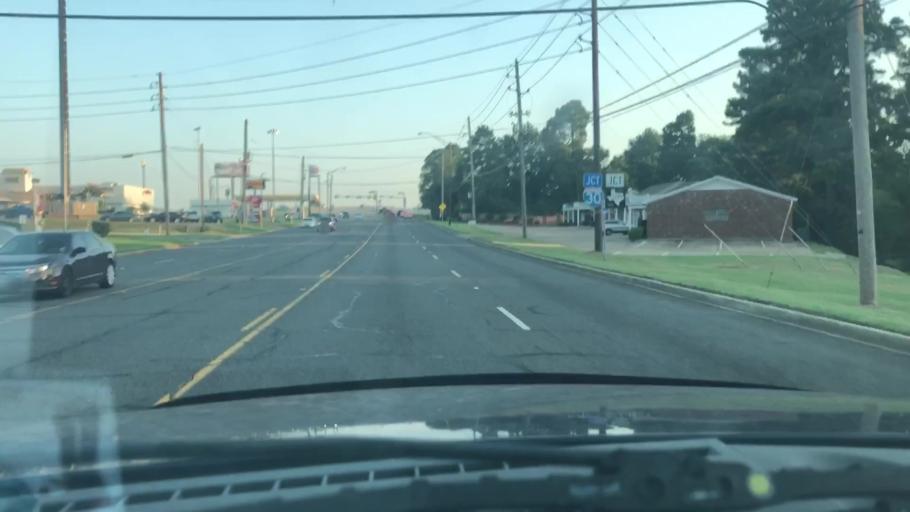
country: US
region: Arkansas
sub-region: Miller County
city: Texarkana
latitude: 33.4613
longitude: -94.0657
